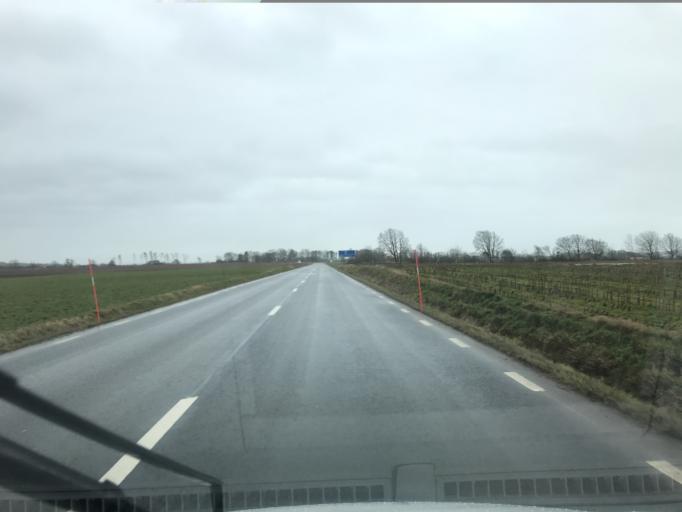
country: SE
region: Skane
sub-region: Bastads Kommun
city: Forslov
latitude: 56.3250
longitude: 12.8879
